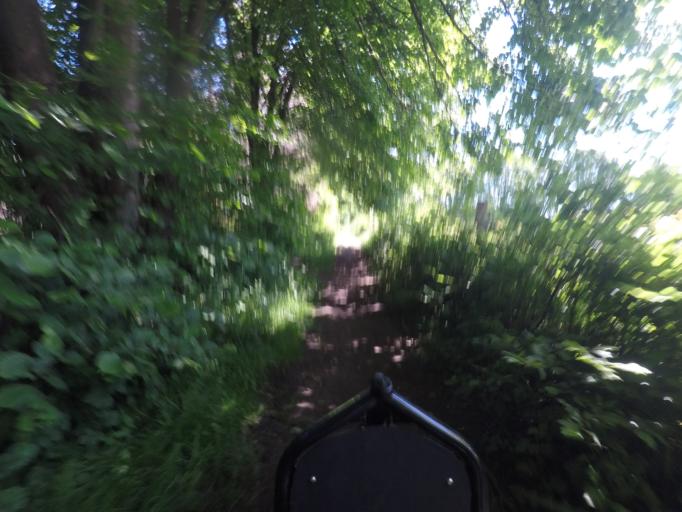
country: DE
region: Schleswig-Holstein
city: Stapelfeld
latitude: 53.6349
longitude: 10.2152
